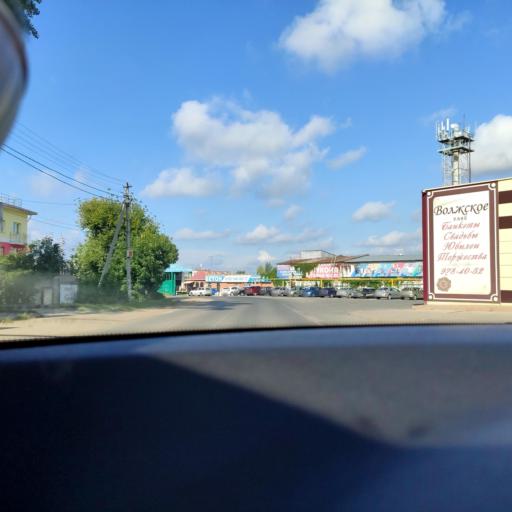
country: RU
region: Samara
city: Volzhskiy
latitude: 53.4341
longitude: 50.0974
